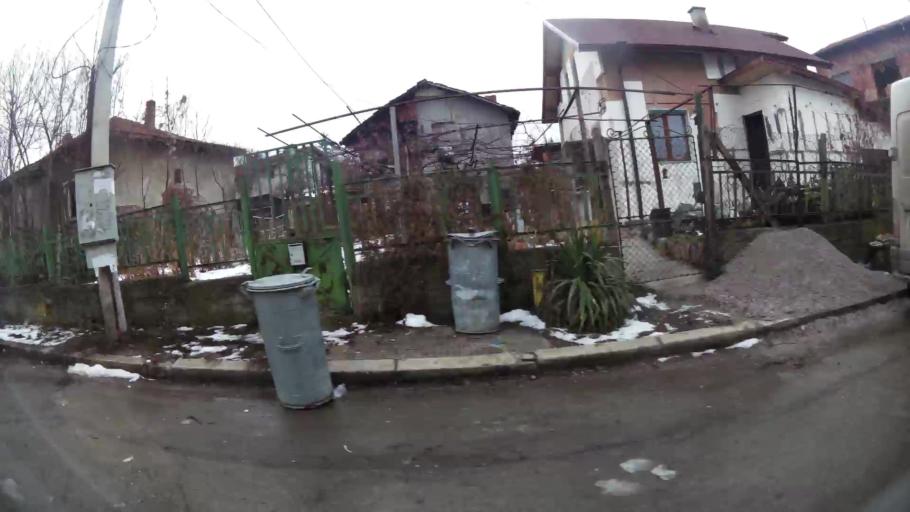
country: BG
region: Sofiya
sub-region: Obshtina Bozhurishte
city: Bozhurishte
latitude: 42.6973
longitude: 23.2235
